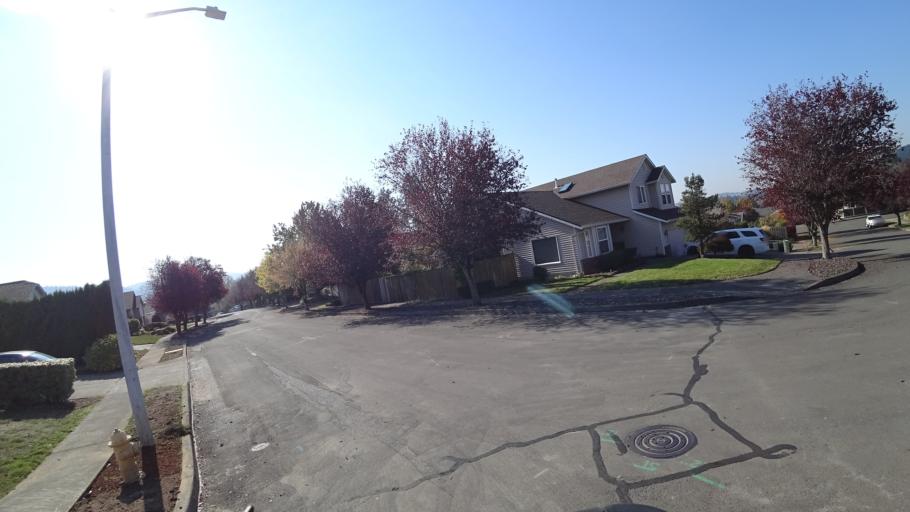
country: US
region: Oregon
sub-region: Multnomah County
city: Gresham
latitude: 45.4955
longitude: -122.4488
